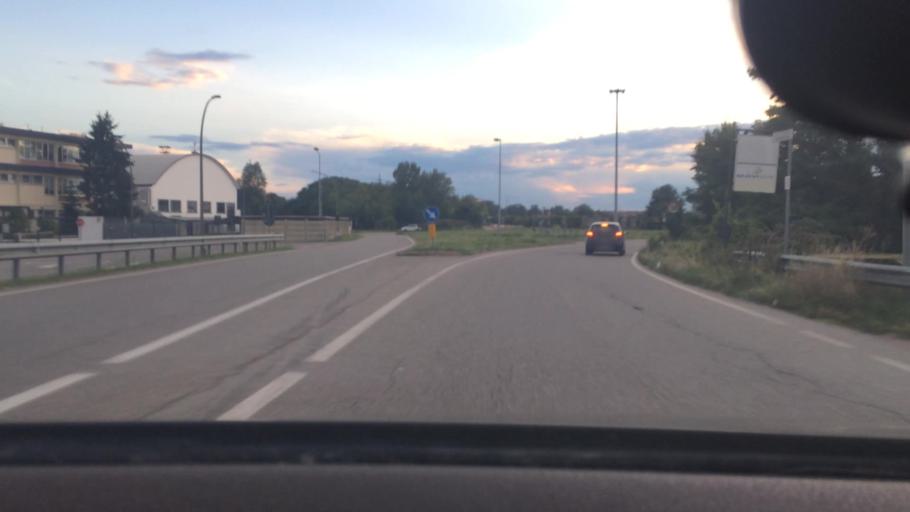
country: IT
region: Lombardy
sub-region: Citta metropolitana di Milano
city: Pregnana Milanese
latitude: 45.5196
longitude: 9.0188
